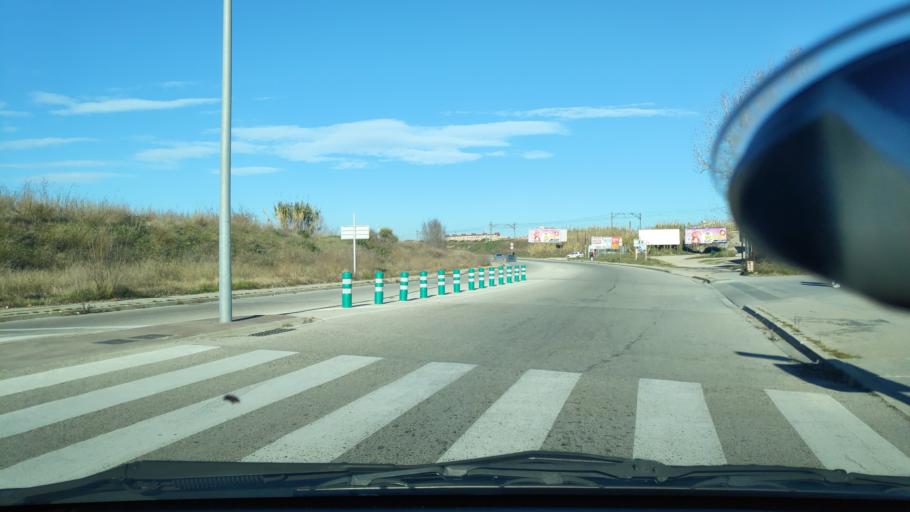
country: ES
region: Catalonia
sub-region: Provincia de Barcelona
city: Barbera del Valles
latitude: 41.5165
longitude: 2.1121
